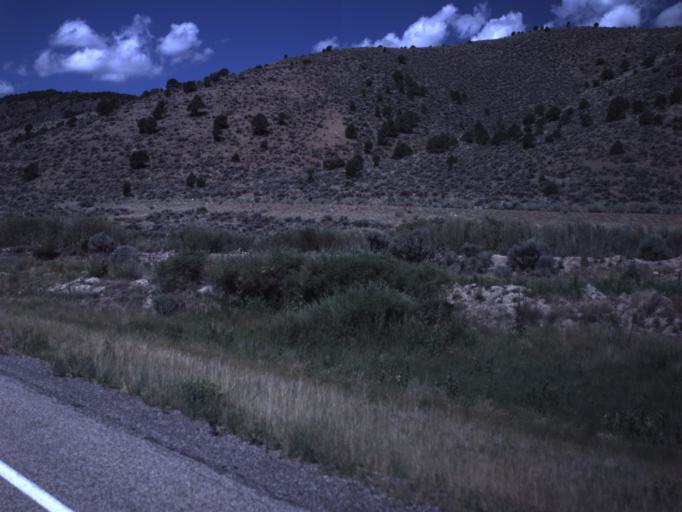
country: US
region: Utah
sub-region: Piute County
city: Junction
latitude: 38.1427
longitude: -112.3062
